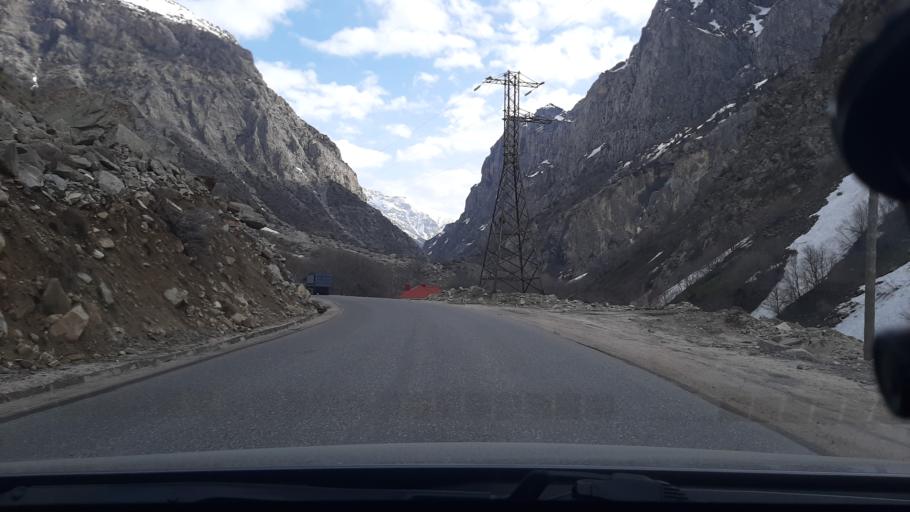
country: TJ
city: Tagob
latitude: 38.9967
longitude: 68.7668
